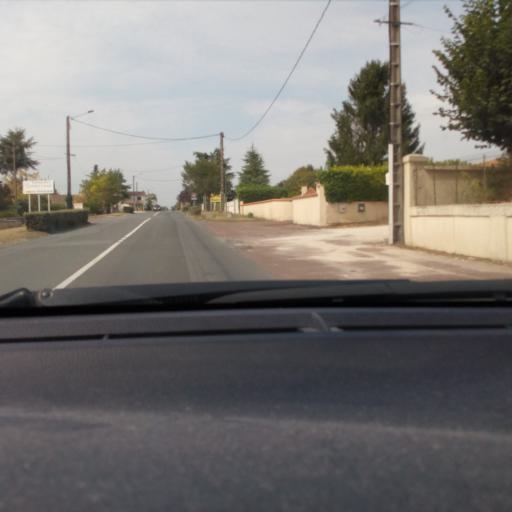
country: FR
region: Poitou-Charentes
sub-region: Departement de la Charente
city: Saint-Yrieix-sur-Charente
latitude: 45.6833
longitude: 0.1134
